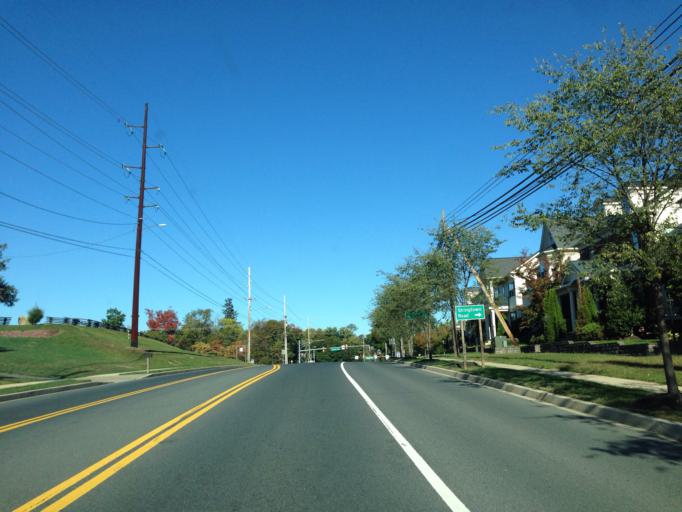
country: US
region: Maryland
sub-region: Montgomery County
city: Clarksburg
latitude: 39.2363
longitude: -77.2762
